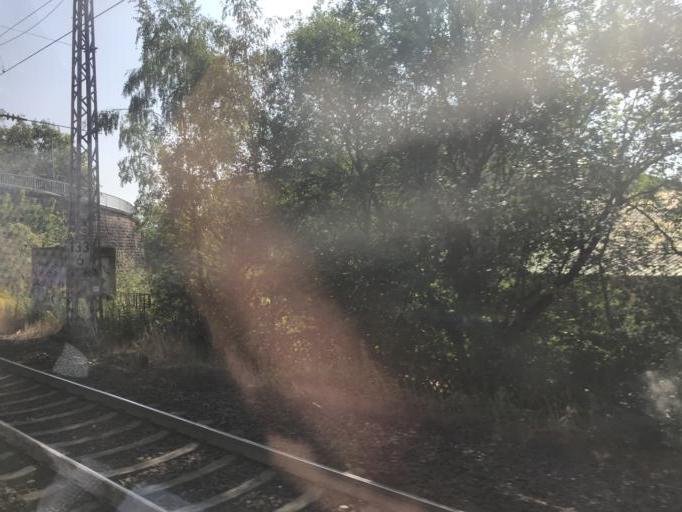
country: DE
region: Saarland
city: Sulzbach
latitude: 49.2967
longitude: 7.0490
